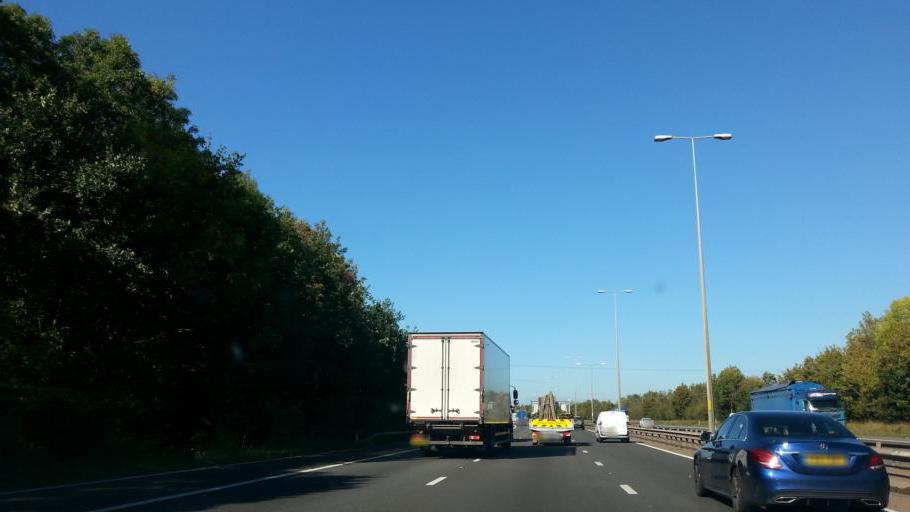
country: GB
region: England
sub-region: Worcestershire
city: Upton upon Severn
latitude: 52.0974
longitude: -2.1860
